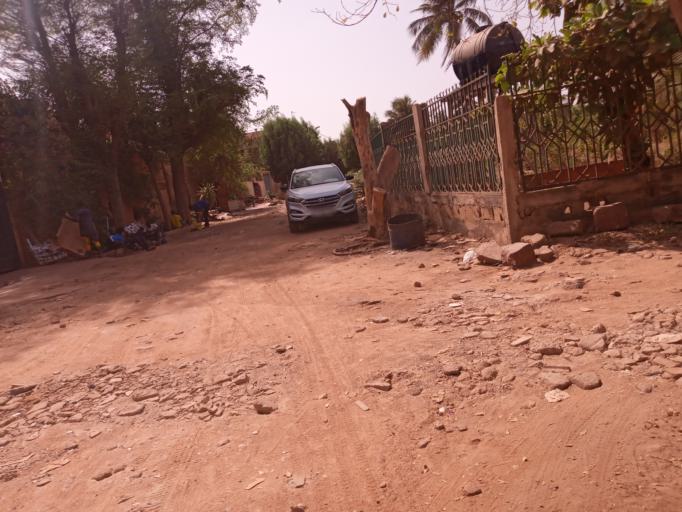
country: ML
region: Bamako
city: Bamako
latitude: 12.5848
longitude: -7.9489
